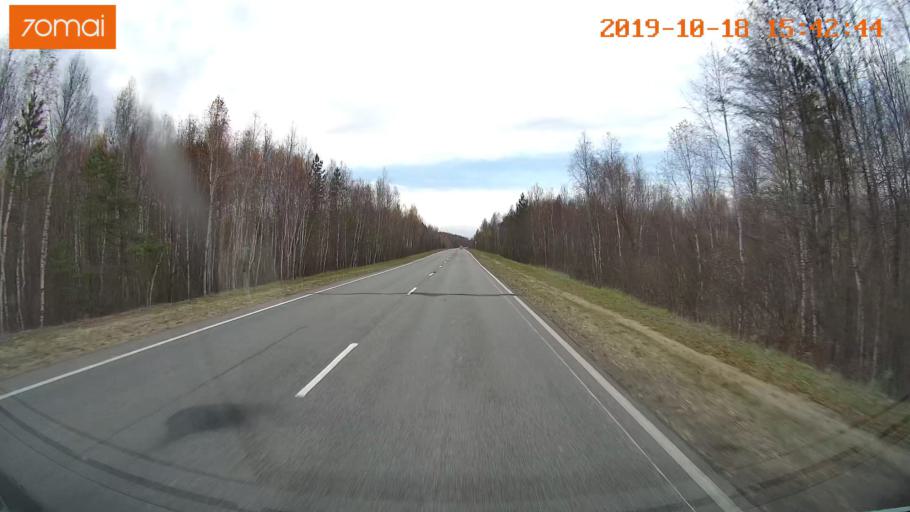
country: RU
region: Vladimir
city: Golovino
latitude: 55.9586
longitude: 40.5630
